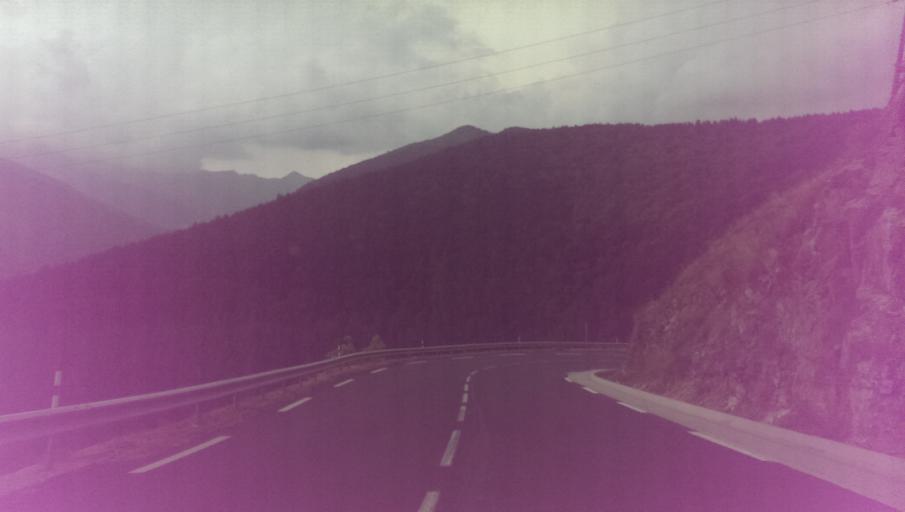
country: ES
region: Catalonia
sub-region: Provincia de Girona
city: Llivia
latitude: 42.5070
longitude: 2.1563
